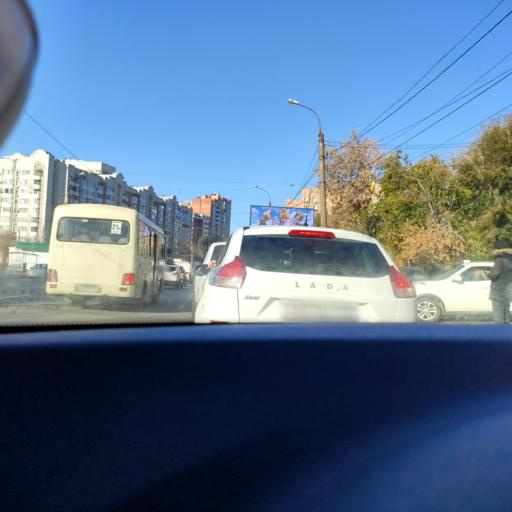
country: RU
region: Samara
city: Samara
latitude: 53.1964
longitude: 50.1584
